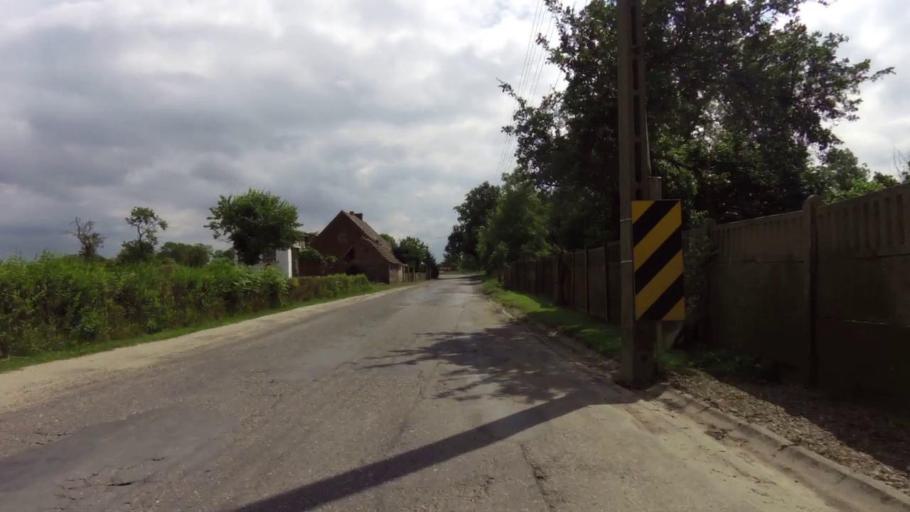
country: PL
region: West Pomeranian Voivodeship
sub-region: Powiat gryfinski
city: Cedynia
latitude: 52.8616
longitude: 14.2648
